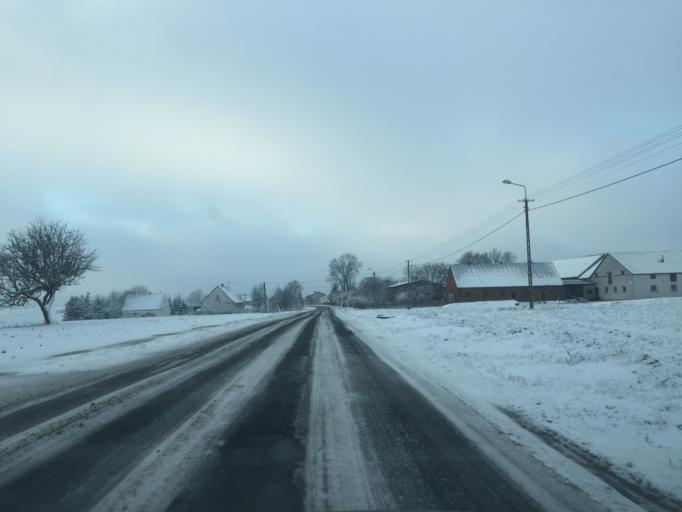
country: PL
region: Kujawsko-Pomorskie
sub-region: Powiat brodnicki
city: Swiedziebnia
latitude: 53.2394
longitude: 19.5032
